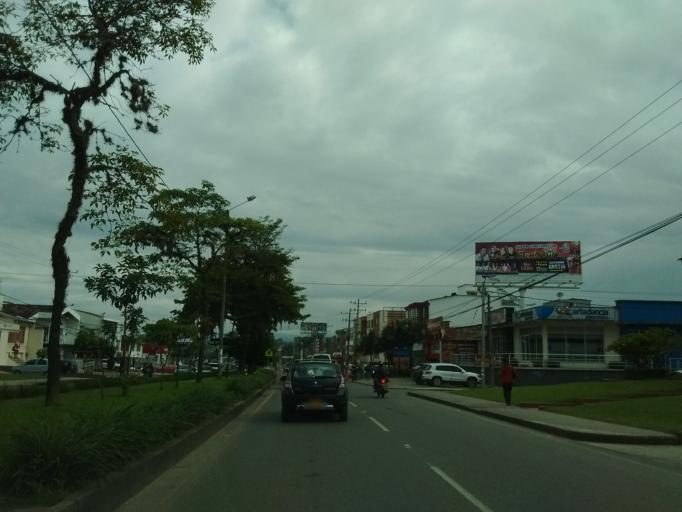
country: CO
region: Cauca
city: Popayan
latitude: 2.4567
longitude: -76.5957
